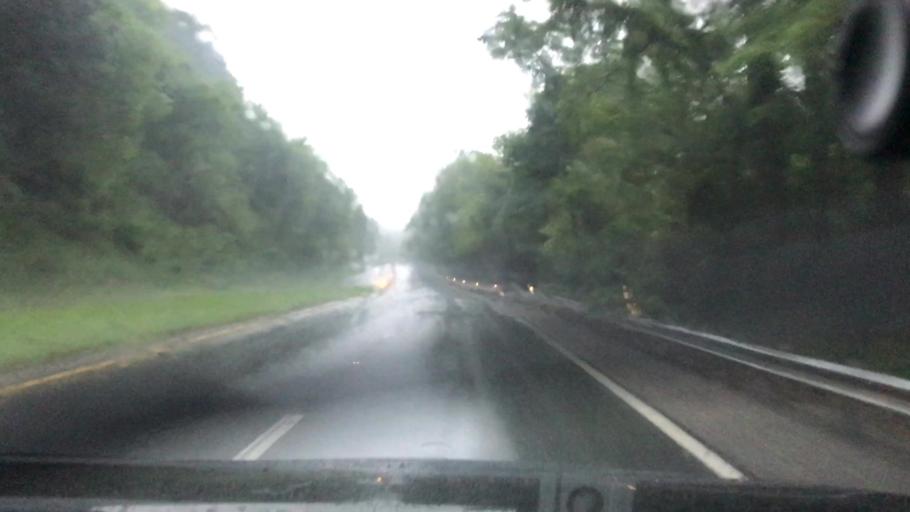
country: US
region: Virginia
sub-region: Giles County
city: Narrows
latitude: 37.3454
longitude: -80.7845
